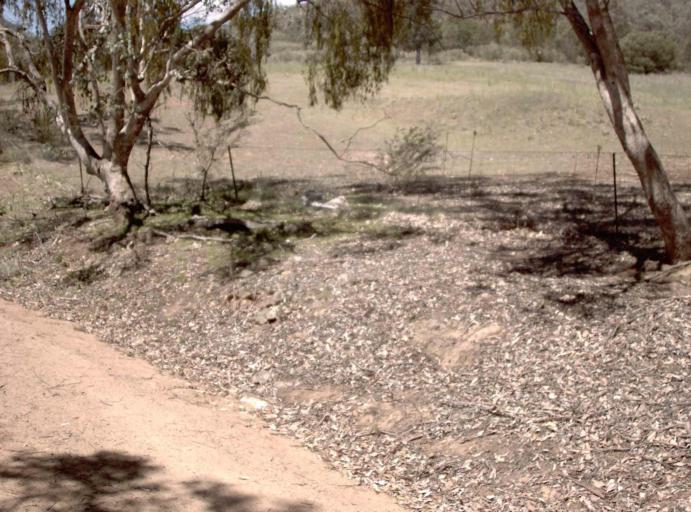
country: AU
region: New South Wales
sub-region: Snowy River
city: Jindabyne
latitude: -37.0653
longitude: 148.5152
